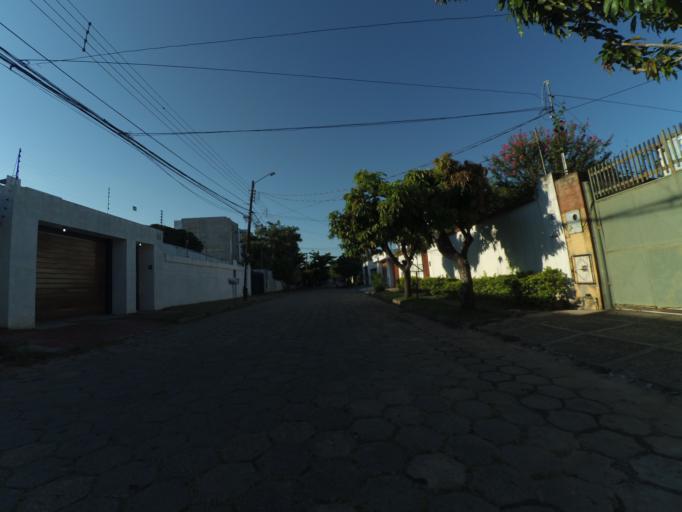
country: BO
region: Santa Cruz
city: Santa Cruz de la Sierra
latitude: -17.7961
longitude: -63.1988
